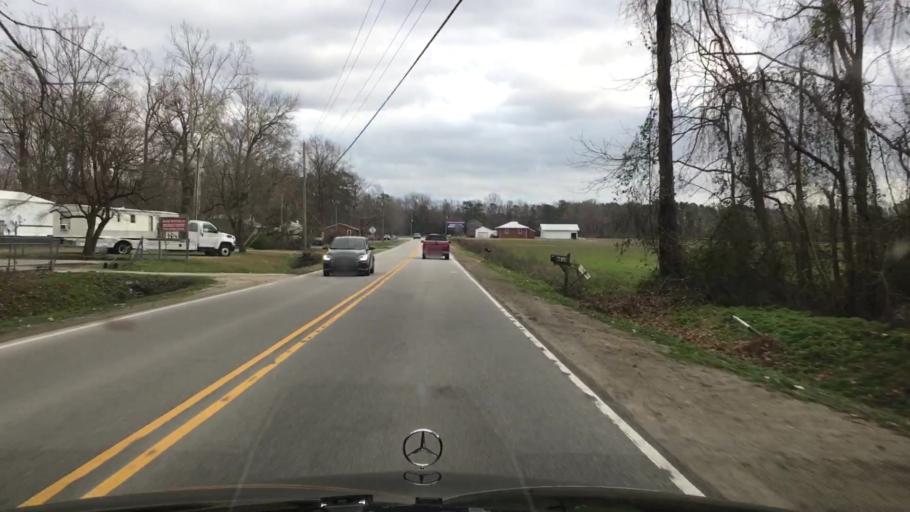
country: US
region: North Carolina
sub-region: Onslow County
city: Richlands
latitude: 34.8794
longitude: -77.5197
